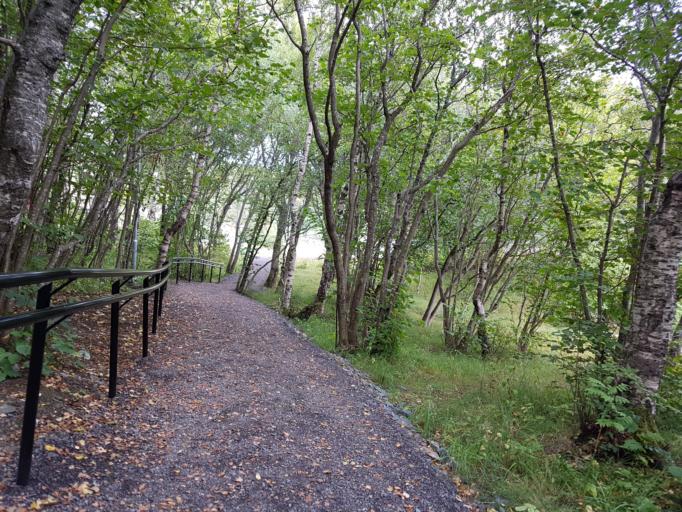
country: NO
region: Sor-Trondelag
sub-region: Trondheim
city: Trondheim
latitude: 63.4468
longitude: 10.4334
